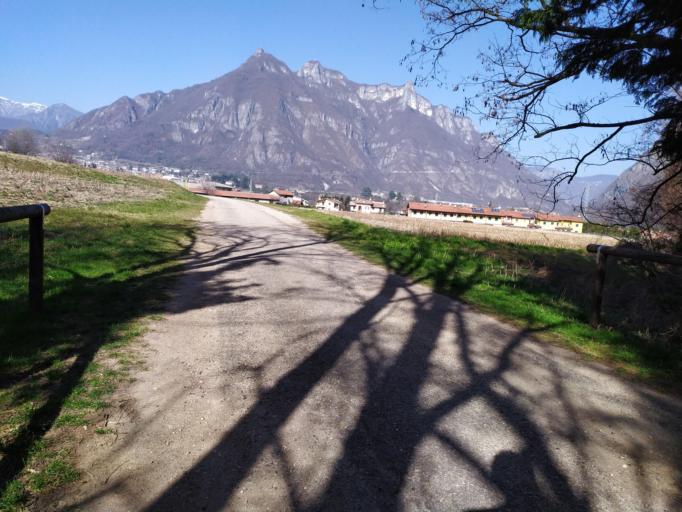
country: IT
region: Veneto
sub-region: Provincia di Vicenza
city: Velo
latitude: 45.7940
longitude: 11.3724
